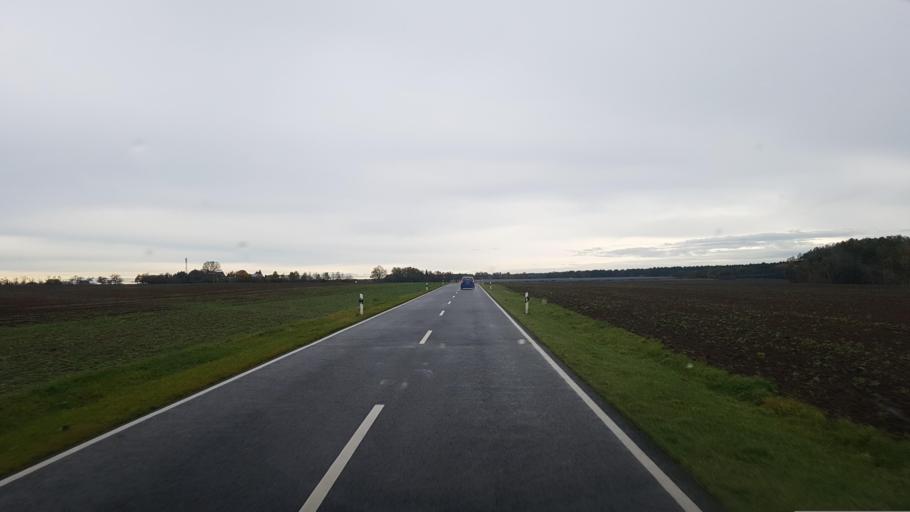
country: DE
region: Saxony-Anhalt
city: Abtsdorf
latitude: 51.9048
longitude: 12.7007
